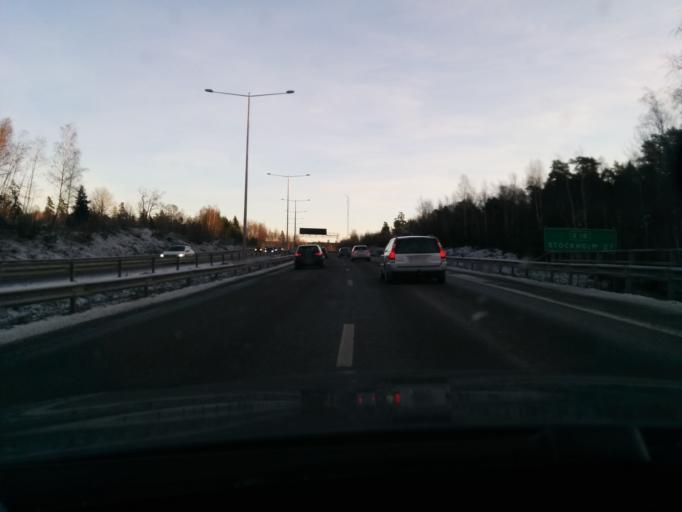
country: SE
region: Stockholm
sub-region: Upplands-Bro Kommun
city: Kungsaengen
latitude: 59.4835
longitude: 17.7662
